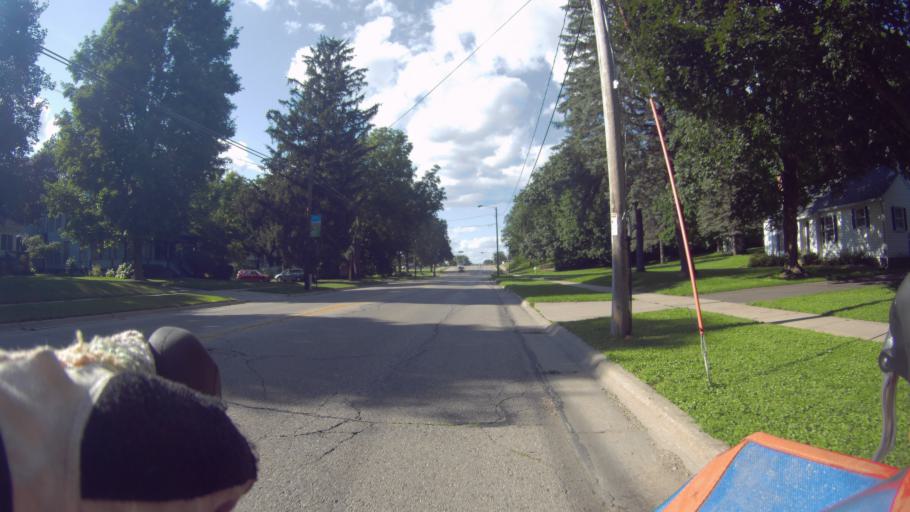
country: US
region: Wisconsin
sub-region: Dane County
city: Oregon
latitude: 42.9344
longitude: -89.3834
